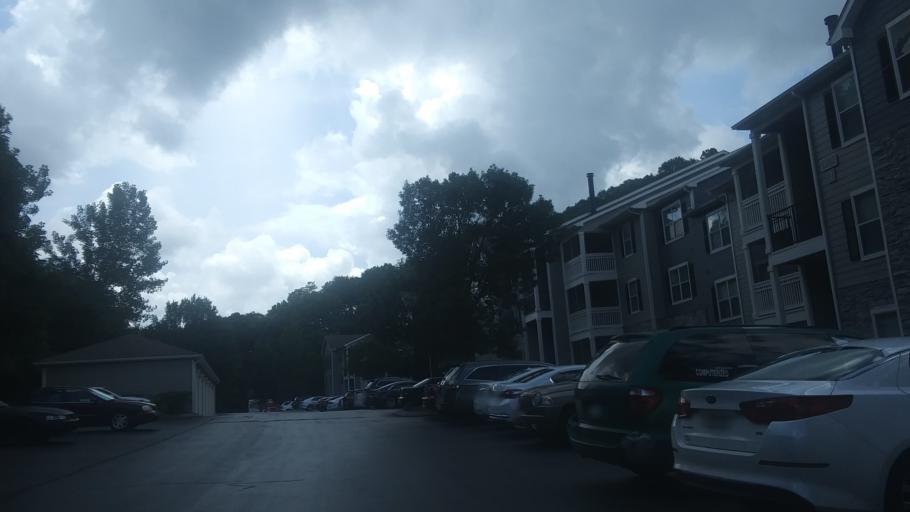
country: US
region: Tennessee
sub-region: Davidson County
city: Belle Meade
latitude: 36.1115
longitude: -86.9165
